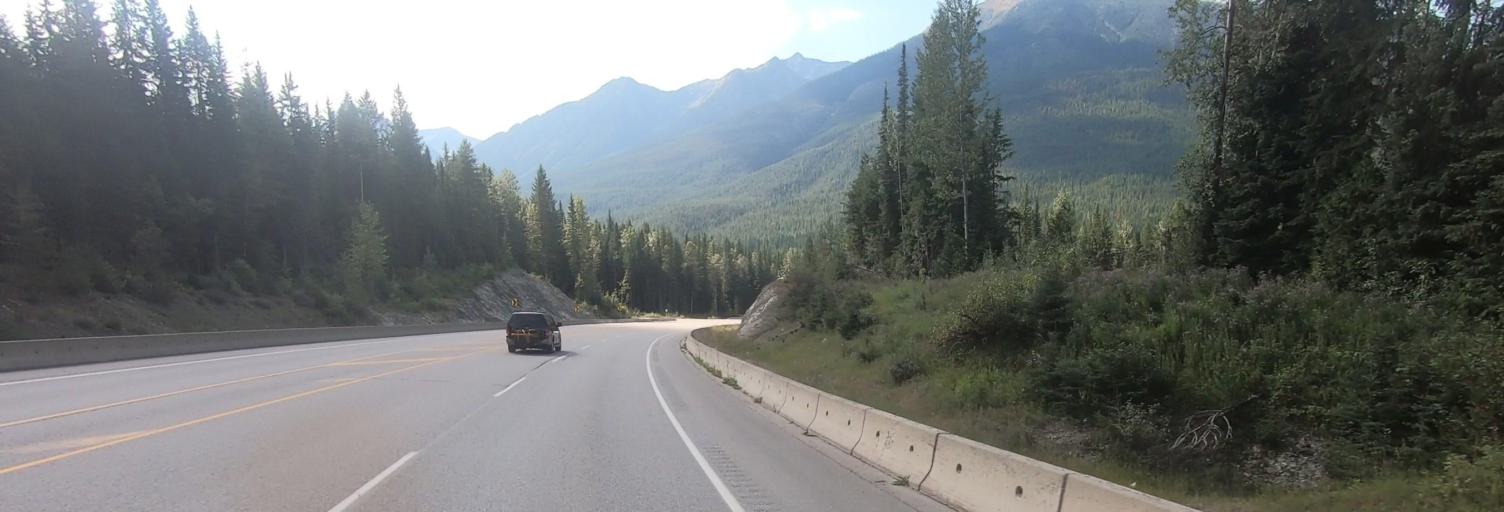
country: CA
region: British Columbia
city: Golden
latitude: 51.4791
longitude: -117.2181
